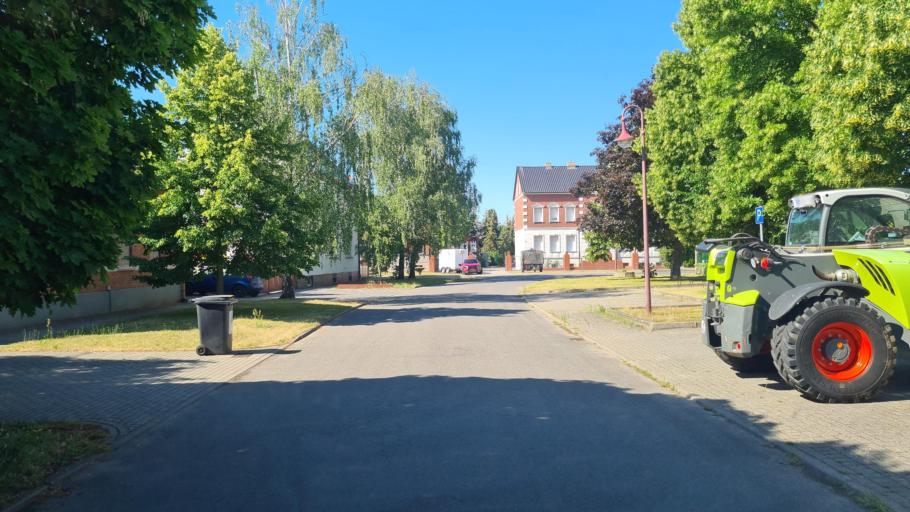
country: DE
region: Saxony-Anhalt
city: Prettin
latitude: 51.6974
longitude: 12.9514
